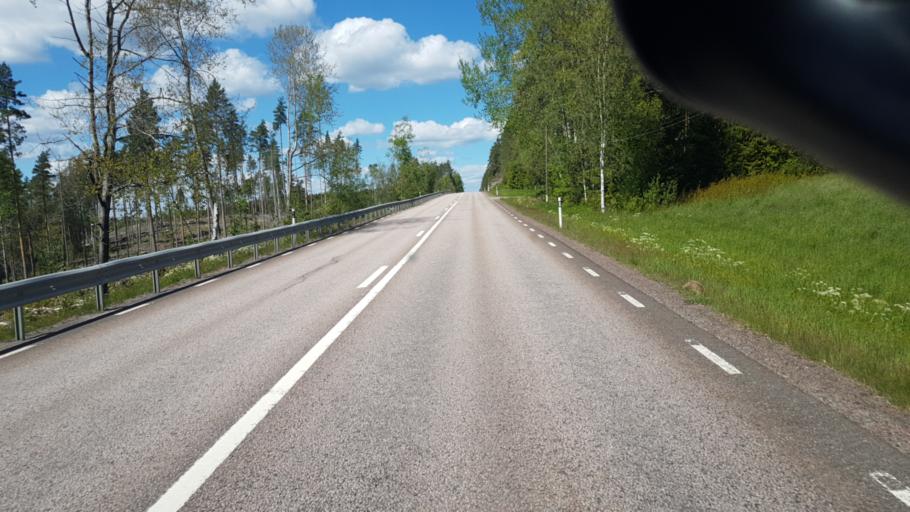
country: SE
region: Vaermland
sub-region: Karlstads Kommun
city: Edsvalla
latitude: 59.5827
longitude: 13.0155
